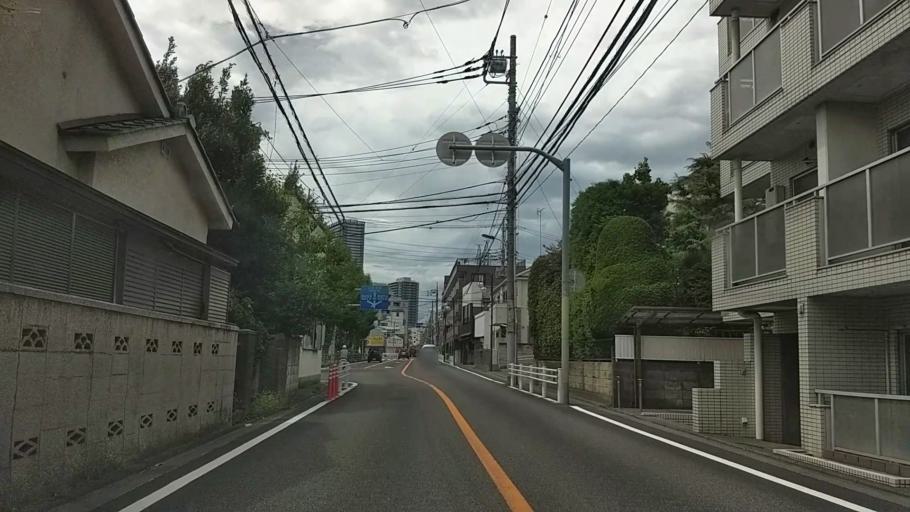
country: JP
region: Tokyo
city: Hachioji
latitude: 35.6506
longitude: 139.3455
